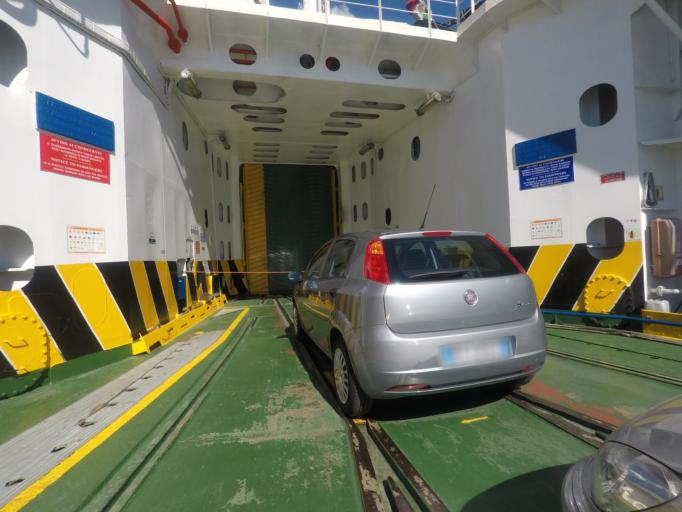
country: IT
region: Sicily
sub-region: Messina
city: Messina
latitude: 38.1888
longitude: 15.5623
